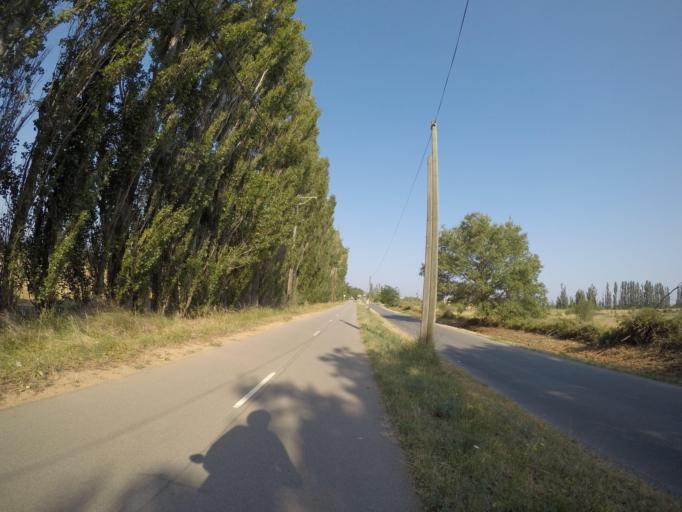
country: FR
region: Languedoc-Roussillon
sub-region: Departement des Pyrenees-Orientales
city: Llupia
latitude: 42.6217
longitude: 2.7781
